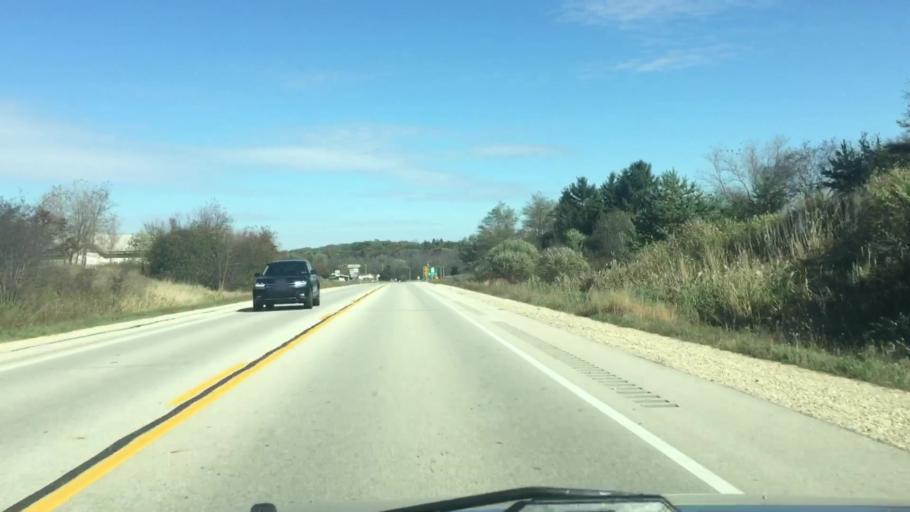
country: US
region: Wisconsin
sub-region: Waukesha County
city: North Prairie
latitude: 42.9539
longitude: -88.3651
